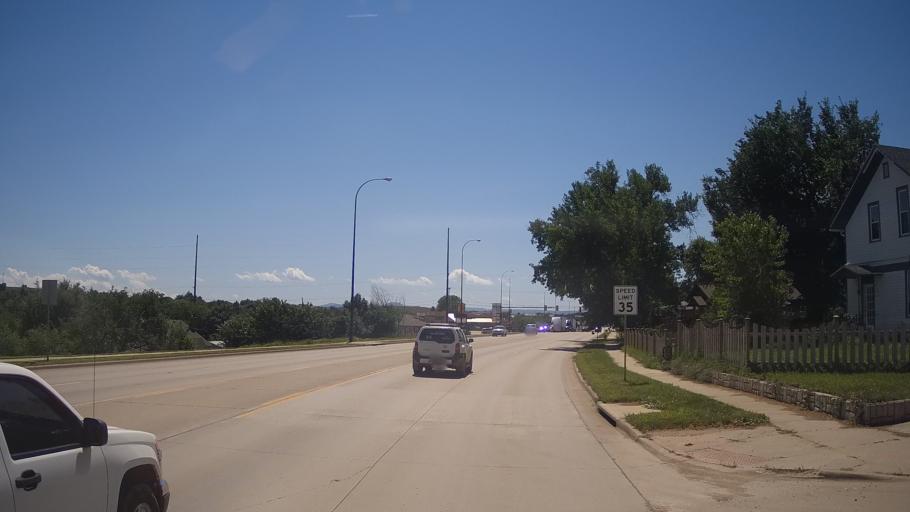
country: US
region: South Dakota
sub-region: Butte County
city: Belle Fourche
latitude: 44.6646
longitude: -103.8539
